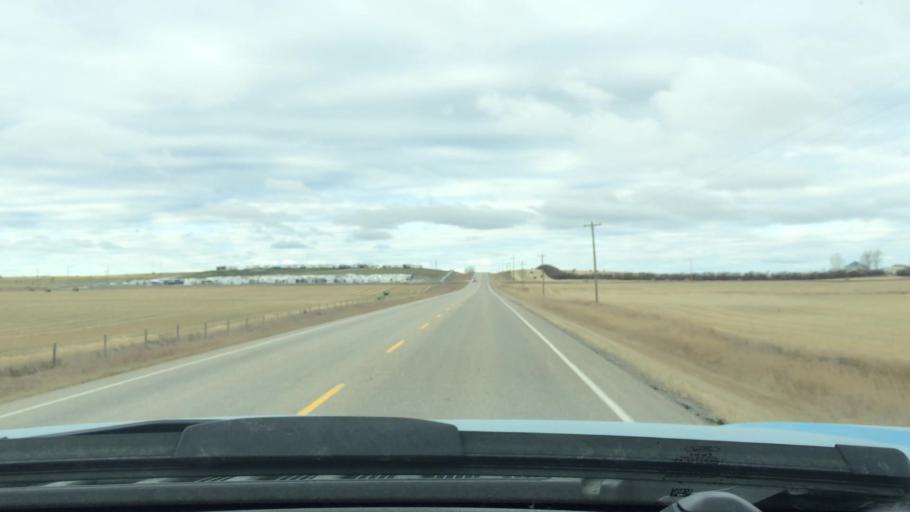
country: CA
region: Alberta
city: Airdrie
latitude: 51.2125
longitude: -114.0423
